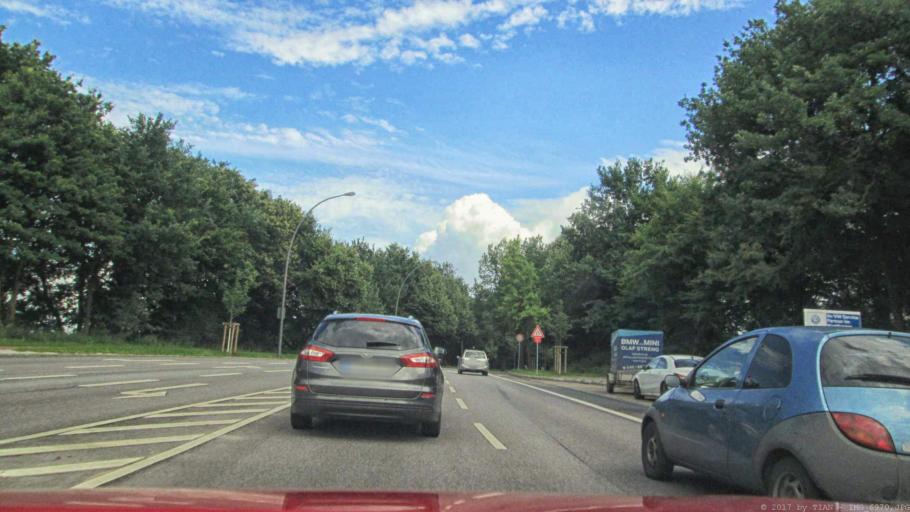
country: DE
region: Schleswig-Holstein
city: Halstenbek
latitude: 53.5747
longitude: 9.8382
